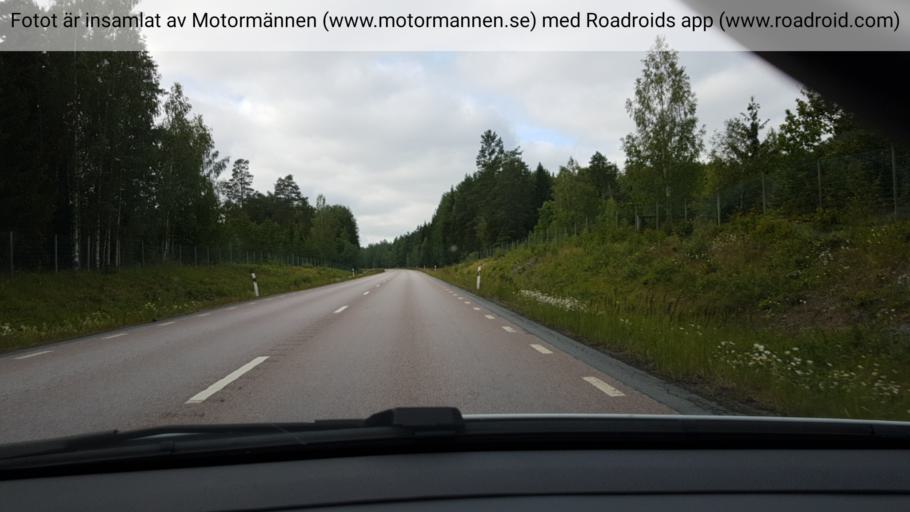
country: SE
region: Uppsala
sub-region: Osthammars Kommun
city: Osterbybruk
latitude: 60.4076
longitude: 17.8700
